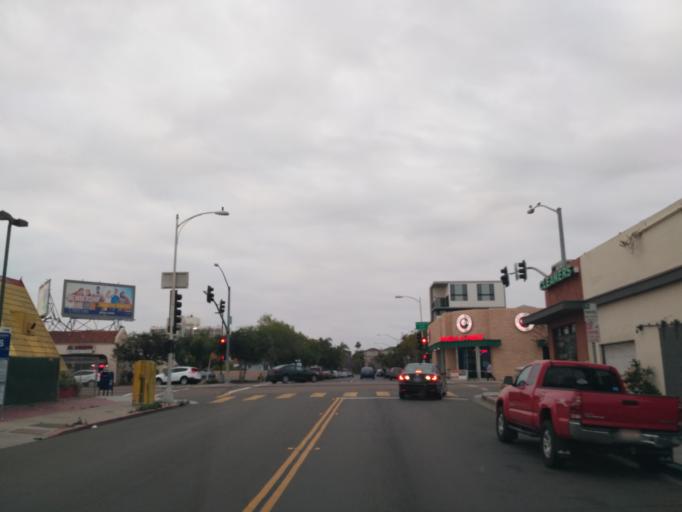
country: US
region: California
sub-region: San Diego County
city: San Diego
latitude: 32.7494
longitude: -117.1639
